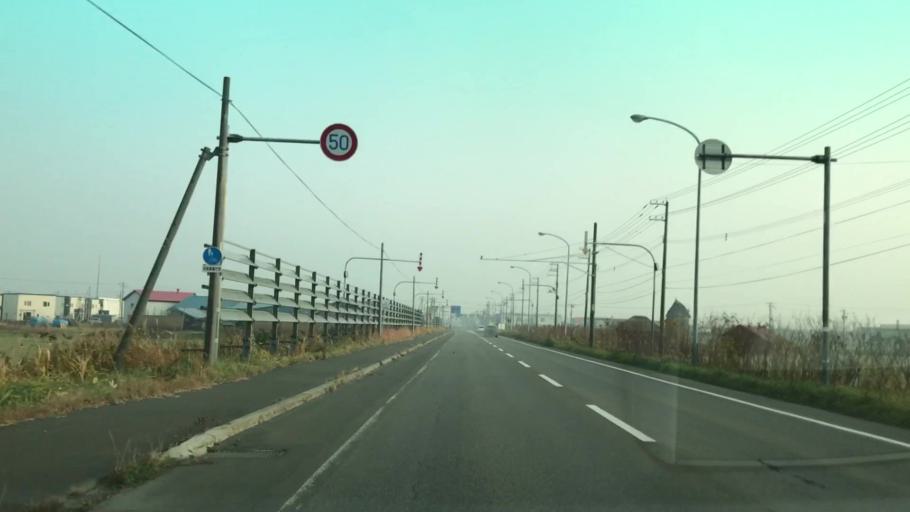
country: JP
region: Hokkaido
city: Ishikari
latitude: 43.2414
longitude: 141.3676
